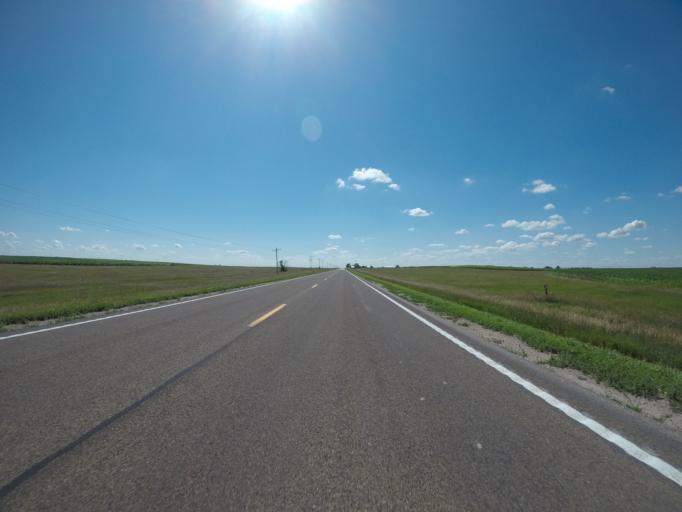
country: US
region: Nebraska
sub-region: Chase County
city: Imperial
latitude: 40.5376
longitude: -101.8437
